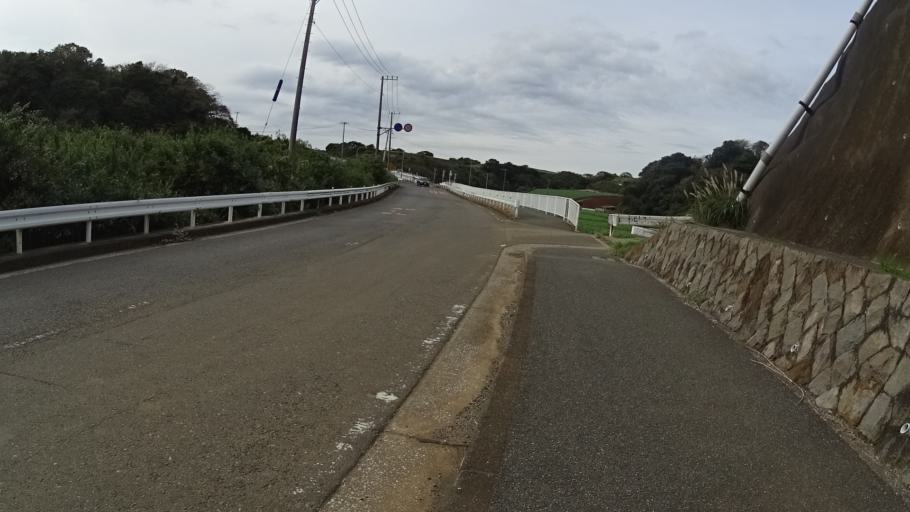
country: JP
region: Kanagawa
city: Miura
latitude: 35.1454
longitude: 139.6617
